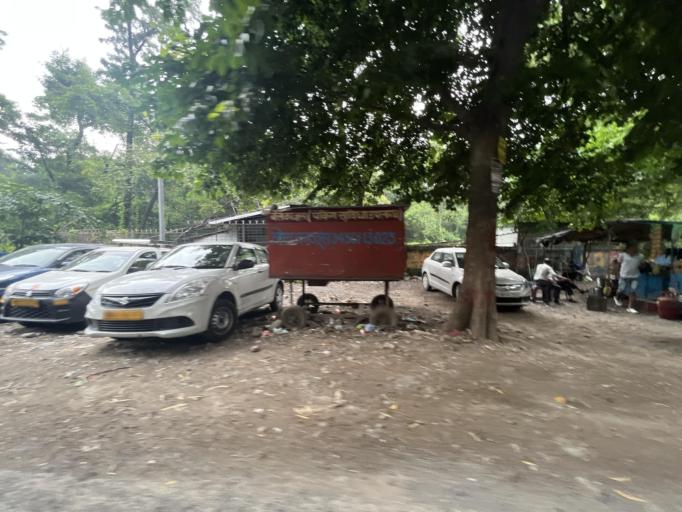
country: IN
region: Uttarakhand
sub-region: Naini Tal
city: Haldwani
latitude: 29.2040
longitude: 79.5169
